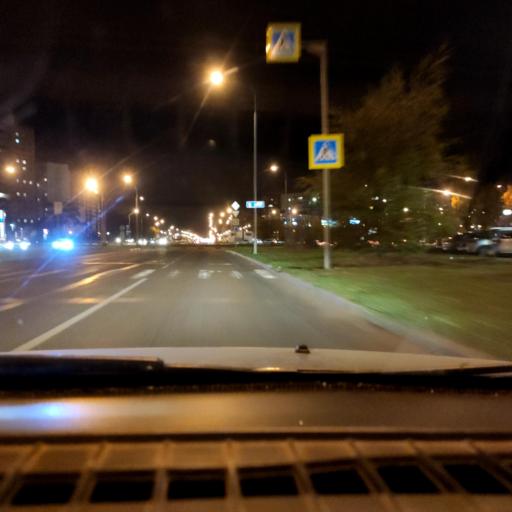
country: RU
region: Samara
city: Tol'yatti
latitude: 53.5404
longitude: 49.3617
